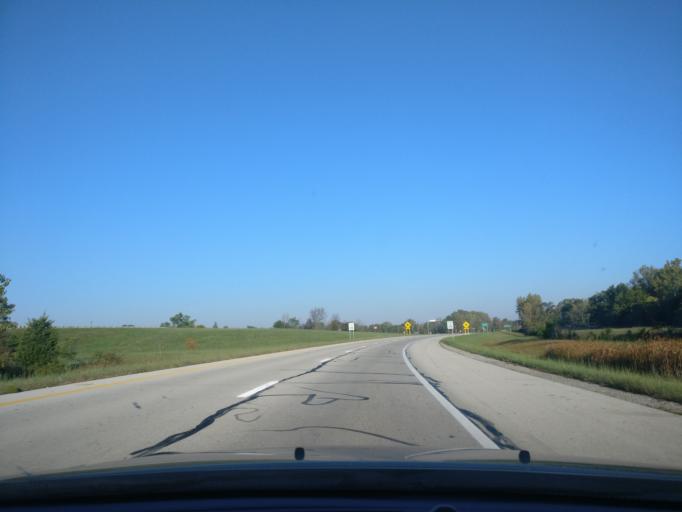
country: US
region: Ohio
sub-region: Montgomery County
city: Clayton
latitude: 39.8555
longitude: -84.3706
